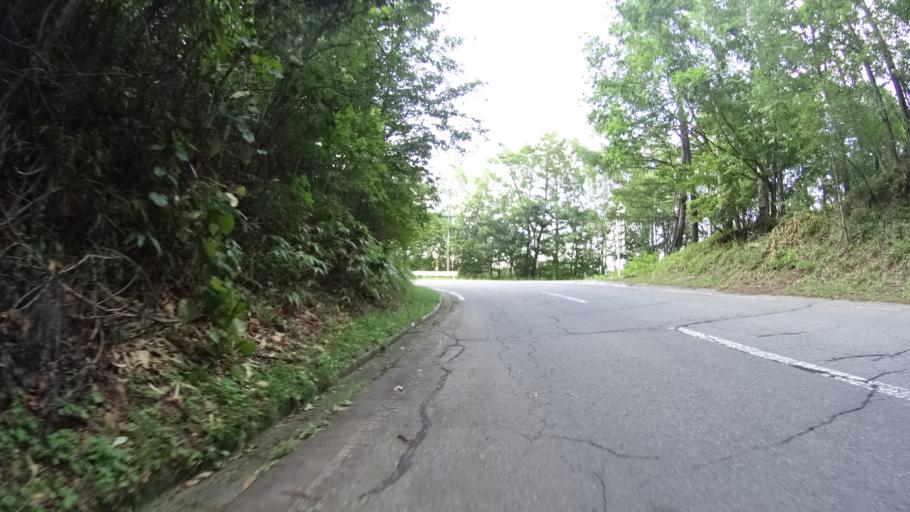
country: JP
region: Nagano
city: Saku
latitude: 36.0534
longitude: 138.4033
